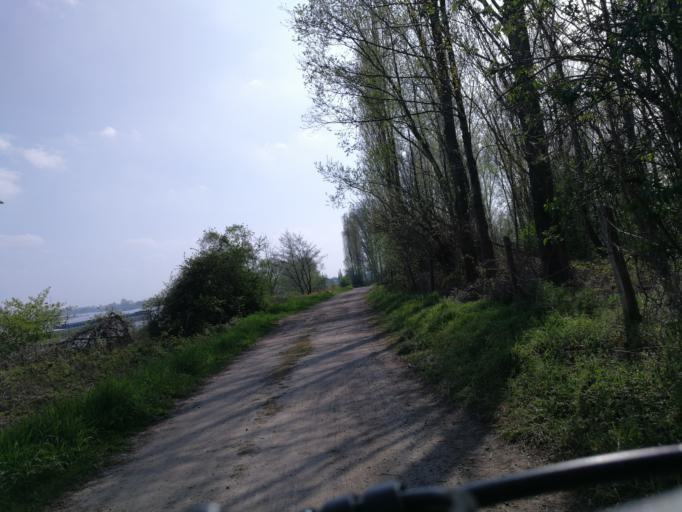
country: DE
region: North Rhine-Westphalia
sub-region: Regierungsbezirk Dusseldorf
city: Dormagen
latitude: 51.1382
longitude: 6.8451
